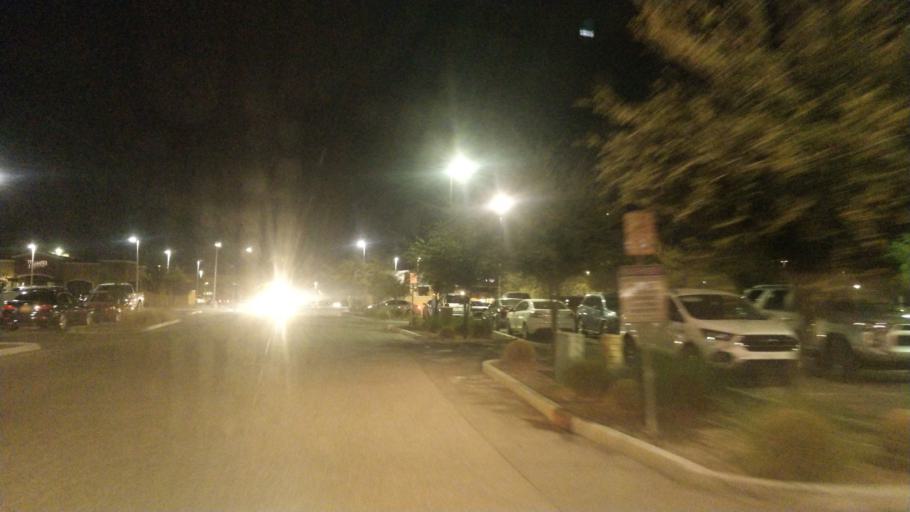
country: US
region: Arizona
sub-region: Maricopa County
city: Sun Lakes
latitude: 33.2480
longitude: -111.8402
